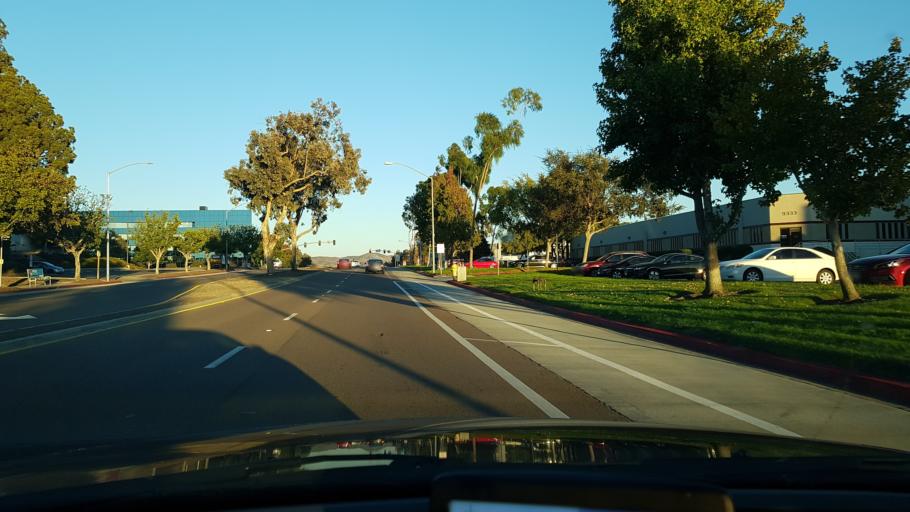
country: US
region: California
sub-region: San Diego County
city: San Diego
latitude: 32.8222
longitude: -117.1299
